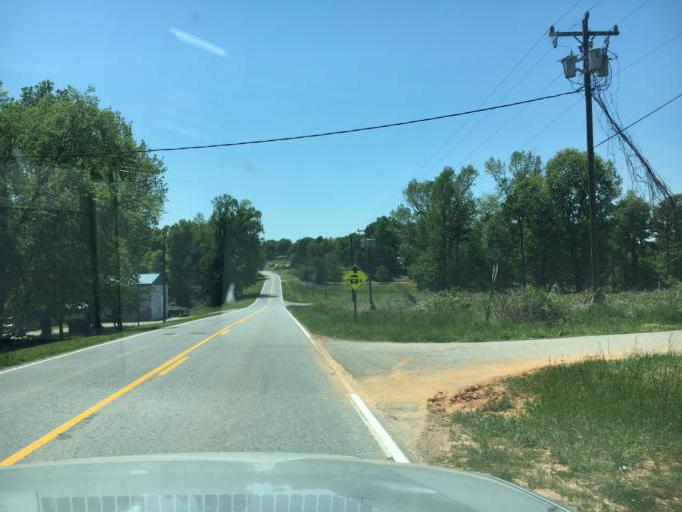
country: US
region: South Carolina
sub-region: Cherokee County
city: East Gaffney
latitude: 35.1194
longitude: -81.5956
